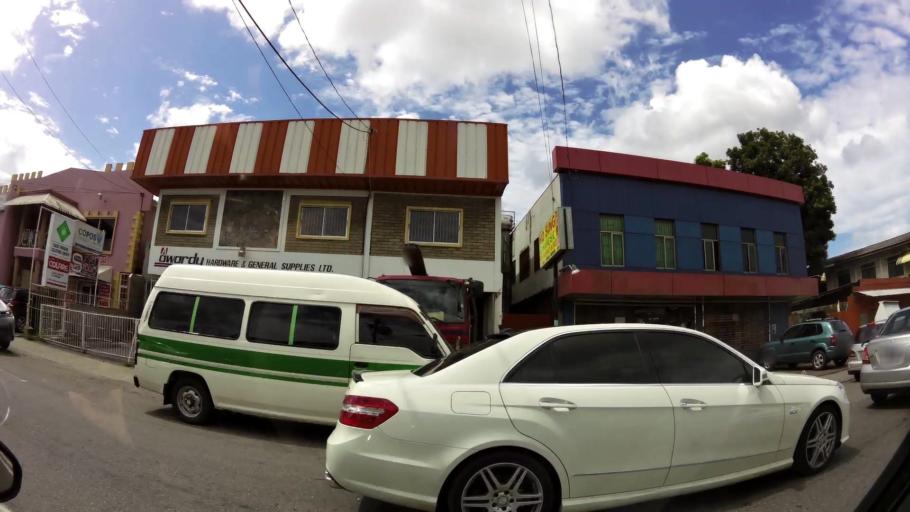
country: TT
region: City of San Fernando
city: Marabella
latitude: 10.3069
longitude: -61.4517
